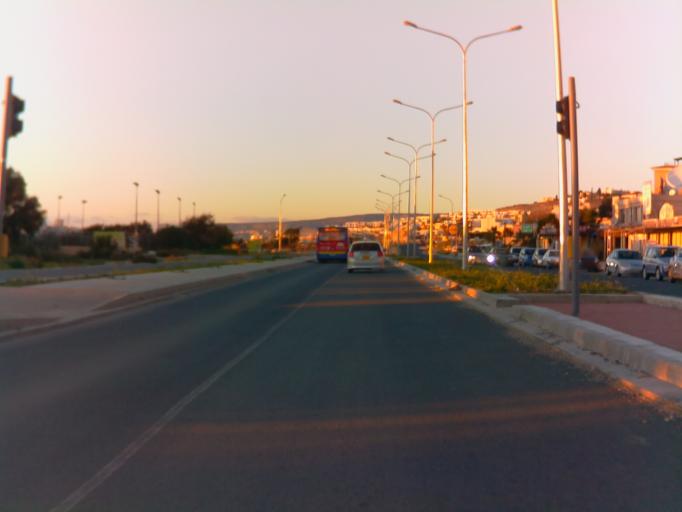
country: CY
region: Pafos
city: Paphos
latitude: 34.7785
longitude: 32.4064
